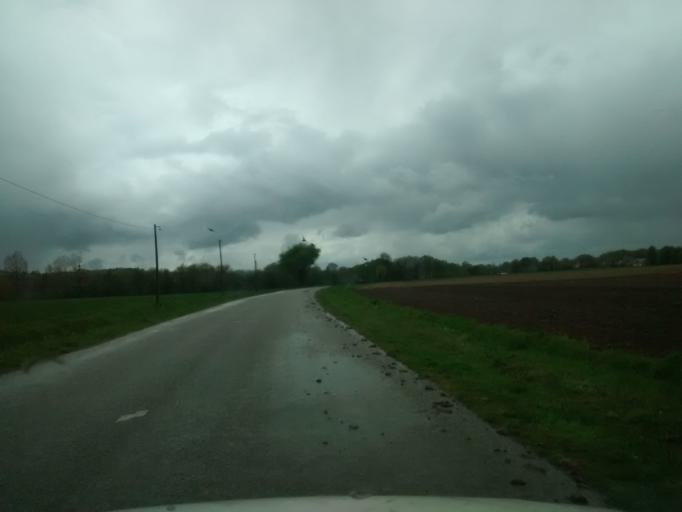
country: FR
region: Brittany
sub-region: Departement du Morbihan
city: Pleucadeuc
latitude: 47.7594
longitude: -2.3201
